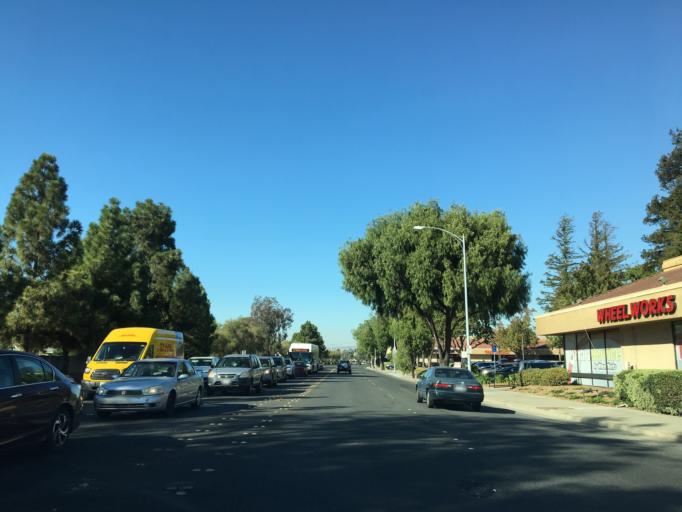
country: US
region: California
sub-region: Santa Clara County
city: Milpitas
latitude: 37.4306
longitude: -121.9090
